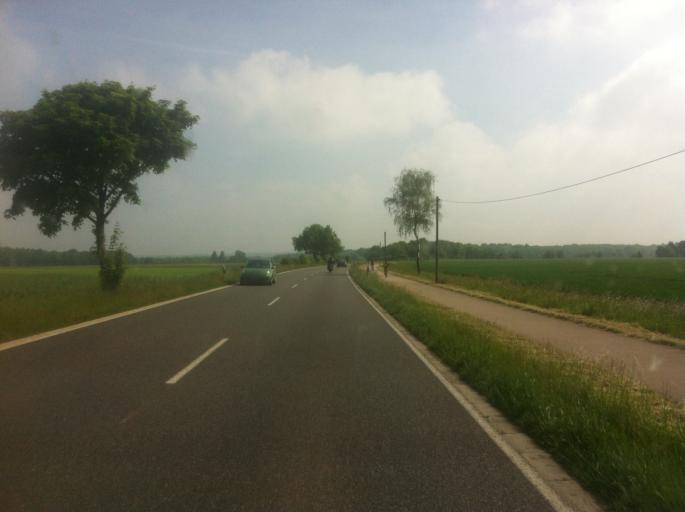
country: DE
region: North Rhine-Westphalia
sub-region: Regierungsbezirk Koln
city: Weilerswist
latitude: 50.7567
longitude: 6.7836
